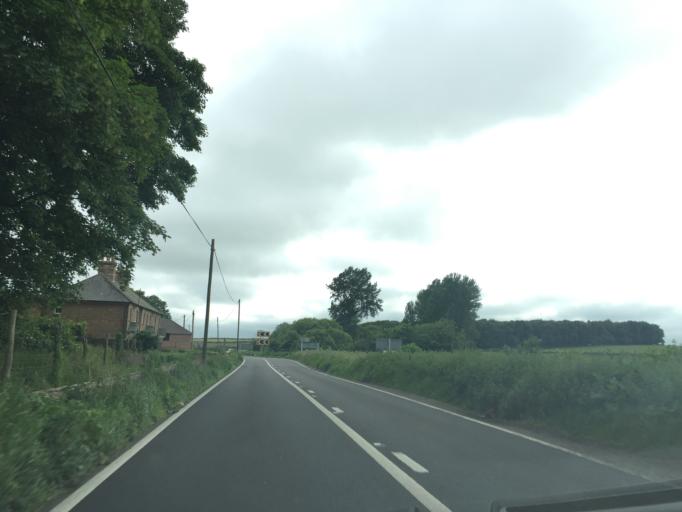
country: GB
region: England
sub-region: Dorset
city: Lytchett Matravers
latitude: 50.7933
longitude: -2.1131
